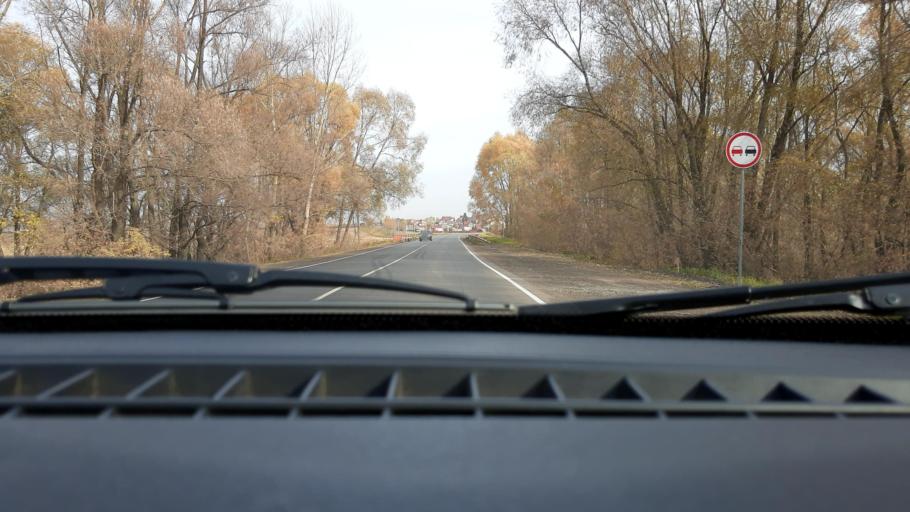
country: RU
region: Bashkortostan
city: Ufa
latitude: 54.8160
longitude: 55.9792
